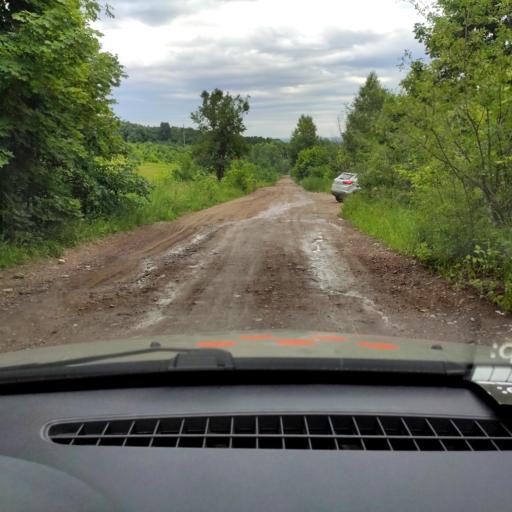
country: RU
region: Bashkortostan
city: Iglino
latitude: 54.8889
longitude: 56.2738
